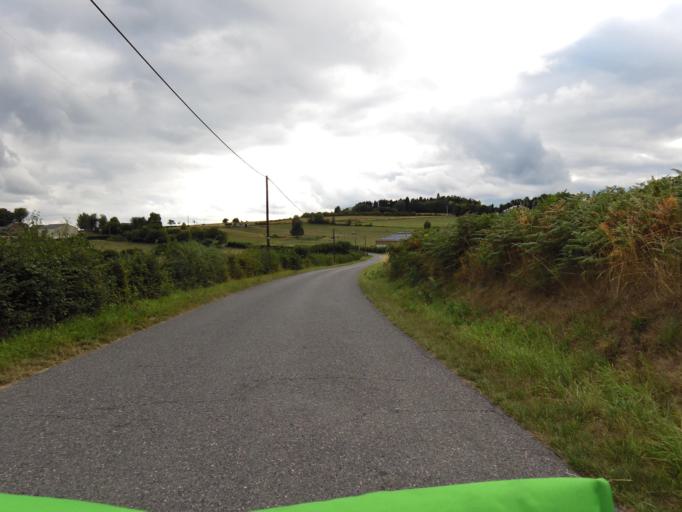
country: BE
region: Wallonia
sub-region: Province de Namur
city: Bievre
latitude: 49.8759
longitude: 4.9836
